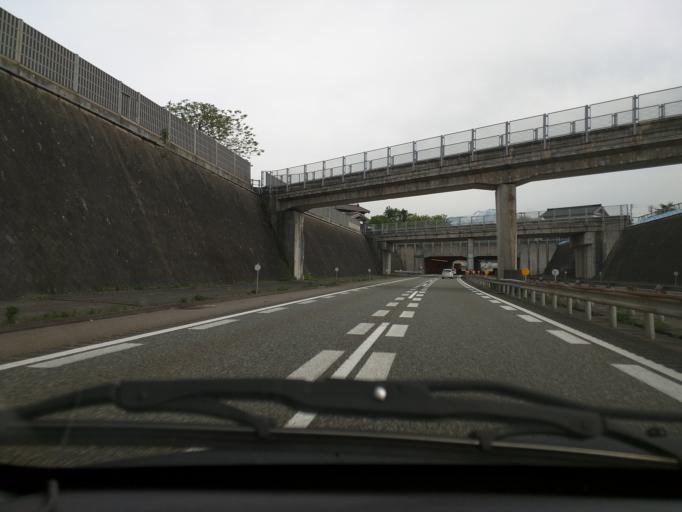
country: JP
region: Niigata
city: Ojiya
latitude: 37.2326
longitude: 138.9759
